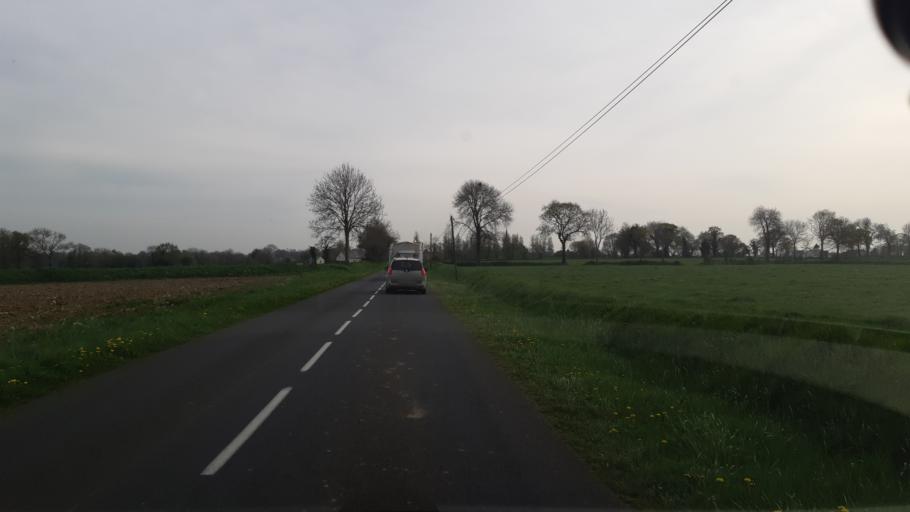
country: FR
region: Lower Normandy
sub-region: Departement de la Manche
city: Cerisy-la-Salle
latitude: 49.0011
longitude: -1.2525
